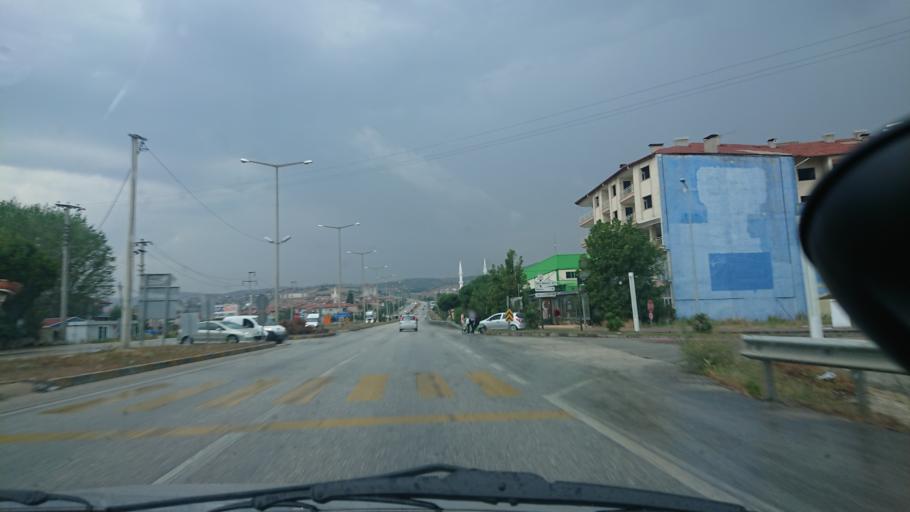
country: TR
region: Manisa
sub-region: Kula
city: Kula
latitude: 38.5415
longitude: 28.6357
